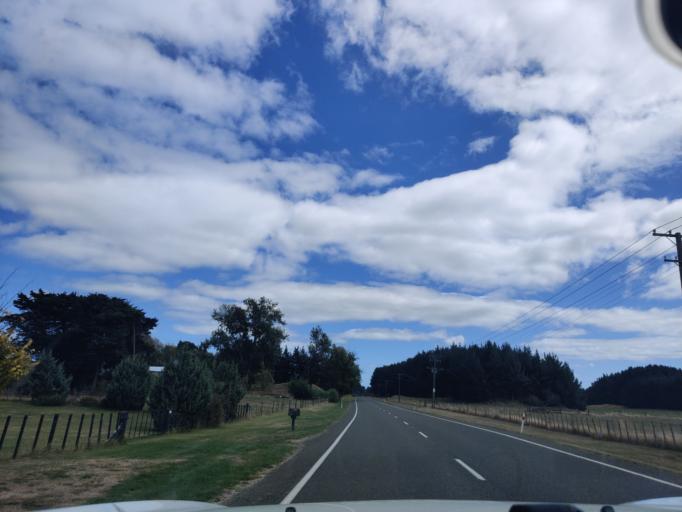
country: NZ
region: Manawatu-Wanganui
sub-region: Horowhenua District
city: Foxton
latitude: -40.4043
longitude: 175.3688
